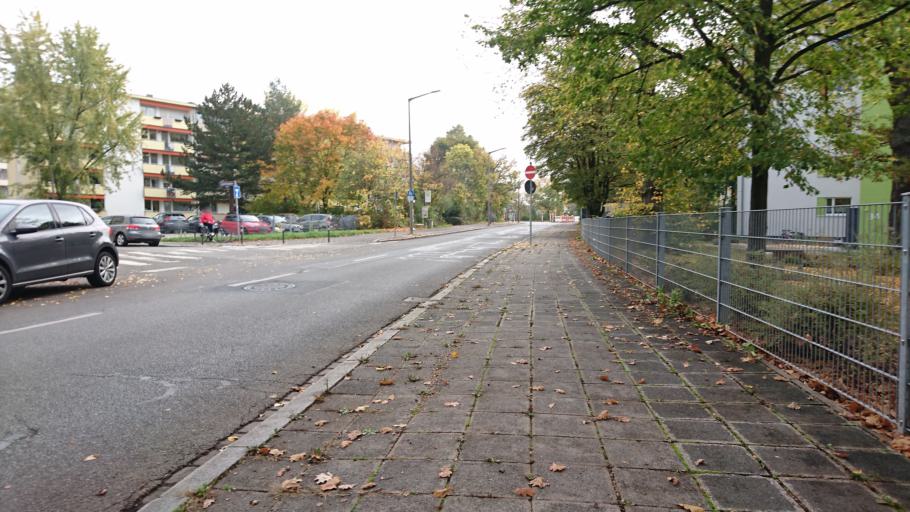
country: DE
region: Bavaria
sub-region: Regierungsbezirk Mittelfranken
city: Nuernberg
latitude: 49.4355
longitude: 11.1116
